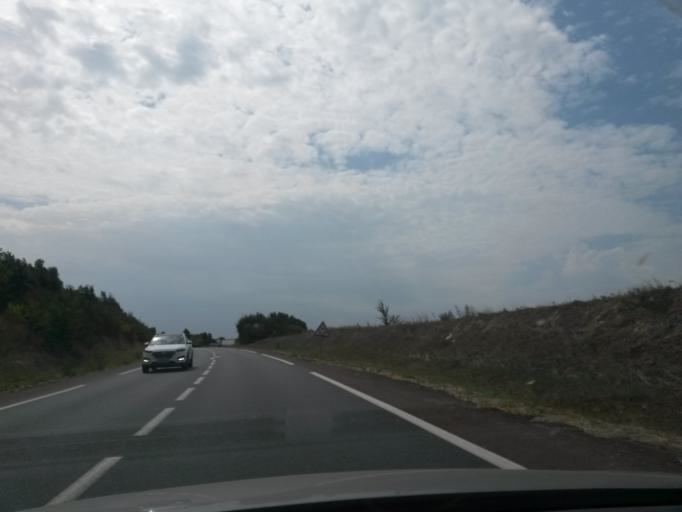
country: FR
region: Poitou-Charentes
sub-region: Departement de la Charente-Maritime
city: Saint-Xandre
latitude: 46.1971
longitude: -1.0955
